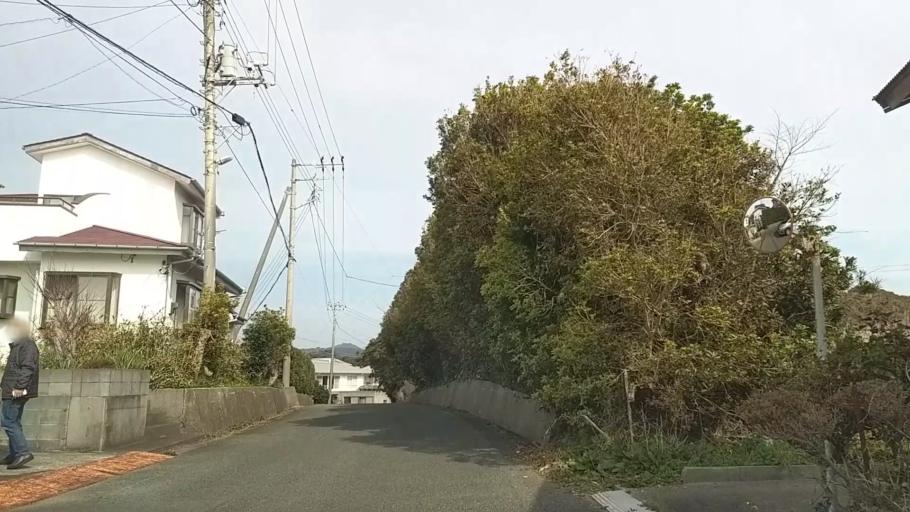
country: JP
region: Shizuoka
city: Shimoda
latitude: 34.6594
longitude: 138.9620
